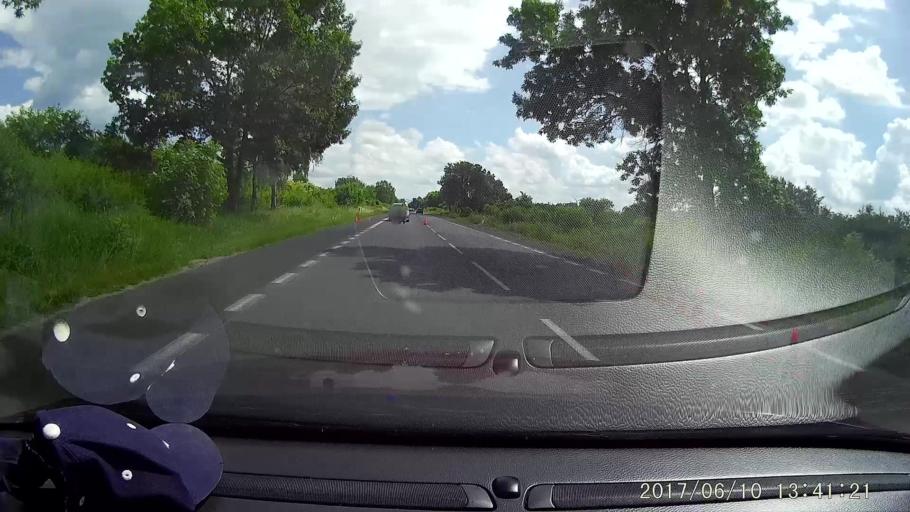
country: PL
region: Lower Silesian Voivodeship
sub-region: Powiat zgorzelecki
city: Zgorzelec
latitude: 51.1026
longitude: 15.0186
